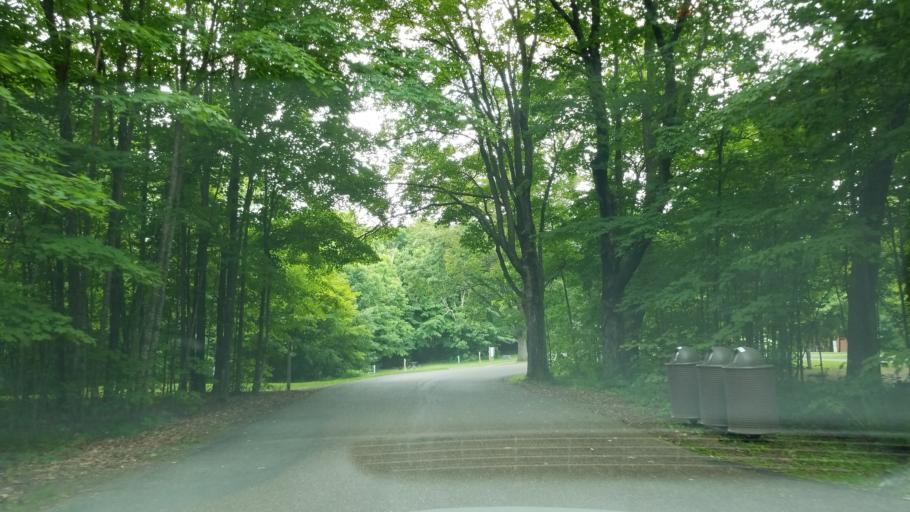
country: US
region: Wisconsin
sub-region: Saint Croix County
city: Glenwood City
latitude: 45.0024
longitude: -92.1672
